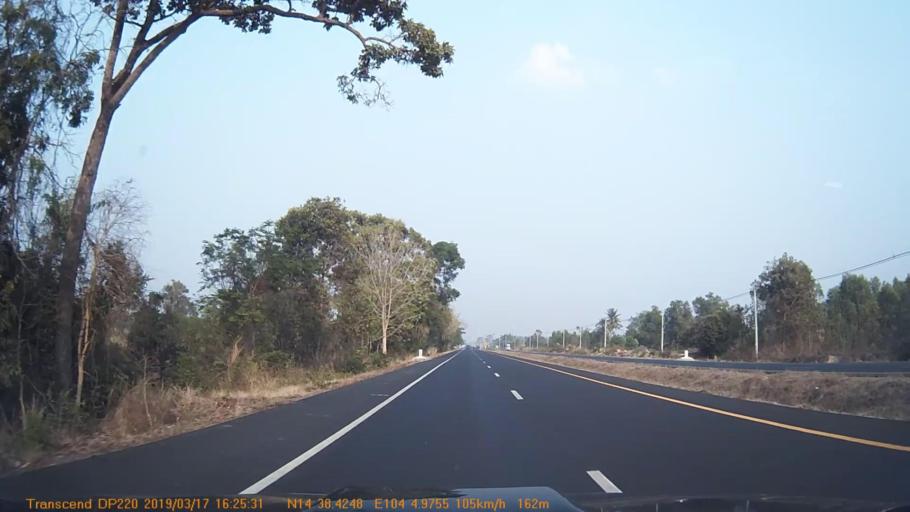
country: TH
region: Sisaket
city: Phu Sing
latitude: 14.6404
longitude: 104.0835
